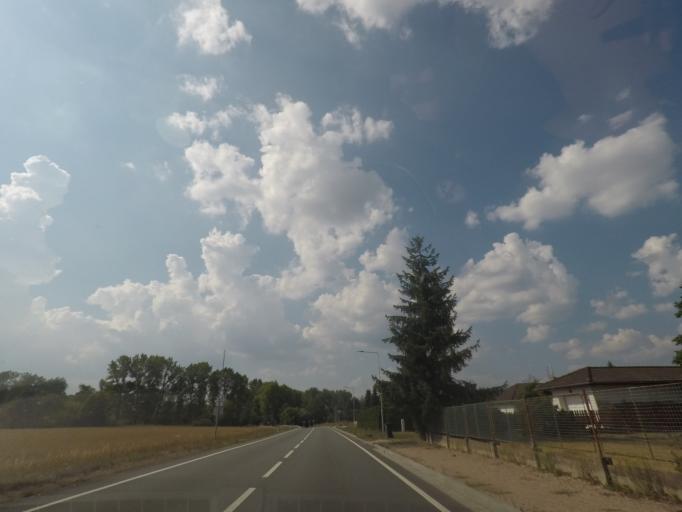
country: CZ
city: Borohradek
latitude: 50.1021
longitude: 16.0872
